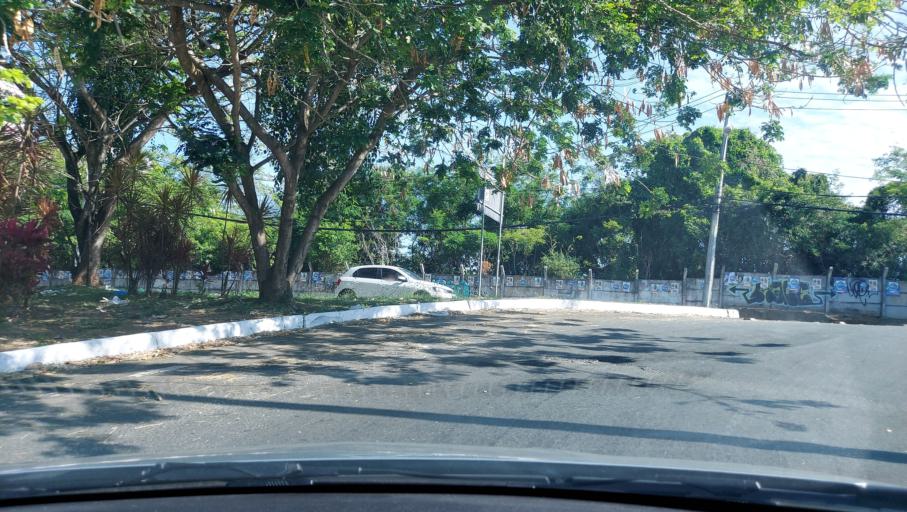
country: BR
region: Bahia
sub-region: Salvador
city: Salvador
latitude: -12.9776
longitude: -38.4446
